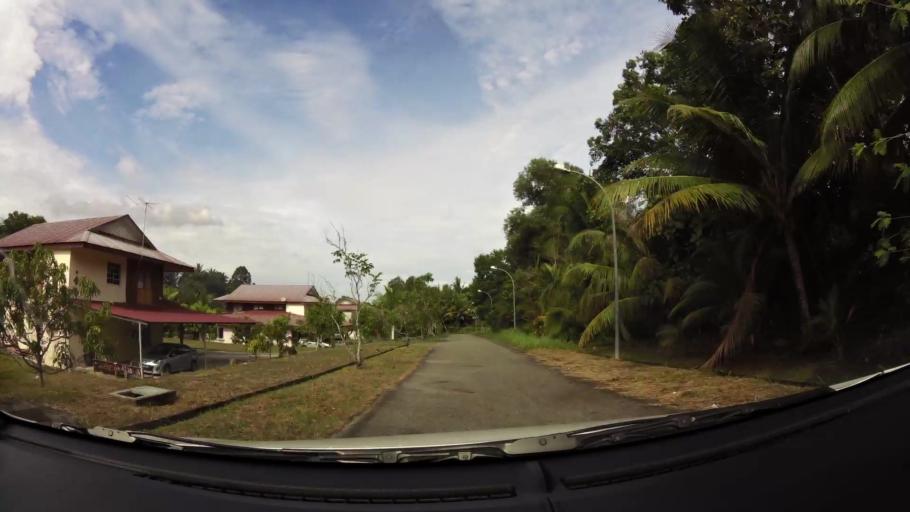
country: BN
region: Brunei and Muara
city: Bandar Seri Begawan
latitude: 4.8956
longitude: 114.8876
